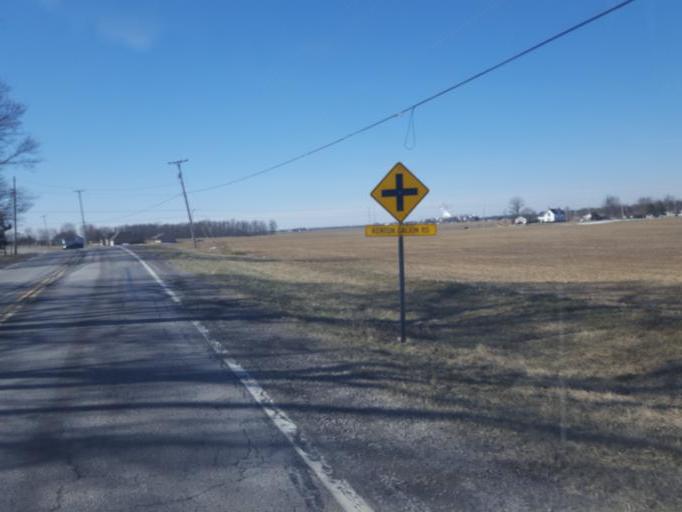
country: US
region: Ohio
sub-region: Marion County
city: Marion
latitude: 40.6462
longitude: -83.1227
